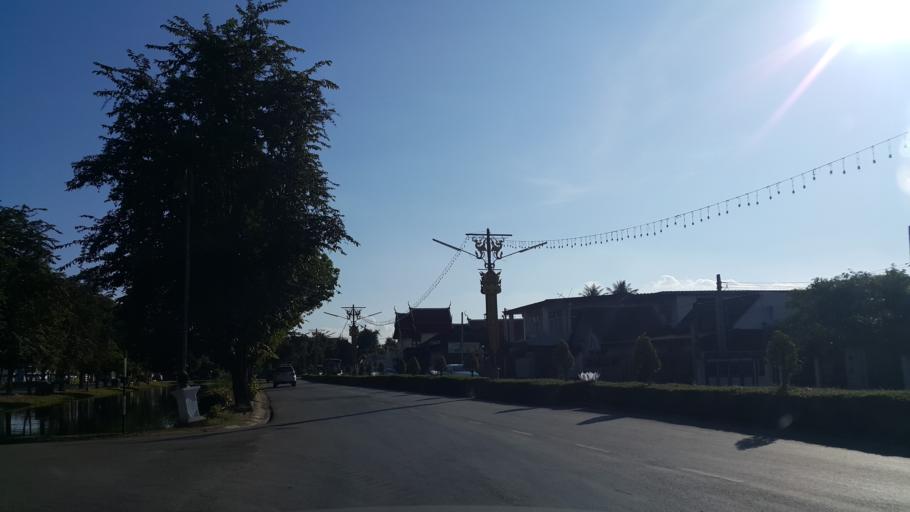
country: TH
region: Lamphun
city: Lamphun
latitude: 18.5743
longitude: 99.0087
